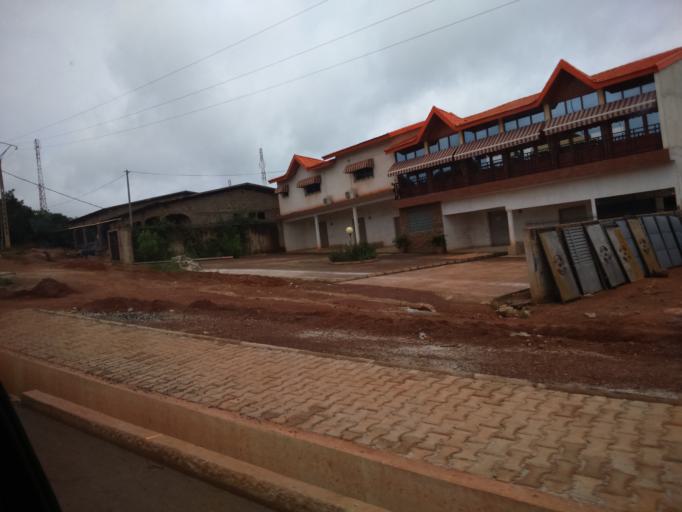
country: CI
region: Moyen-Comoe
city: Abengourou
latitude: 6.7219
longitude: -3.5114
